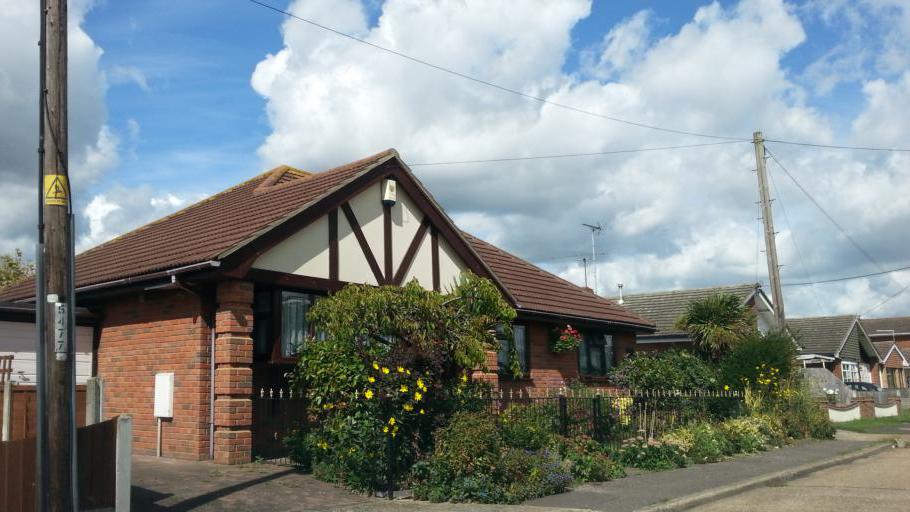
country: GB
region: England
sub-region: Essex
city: Canvey Island
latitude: 51.5231
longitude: 0.5834
